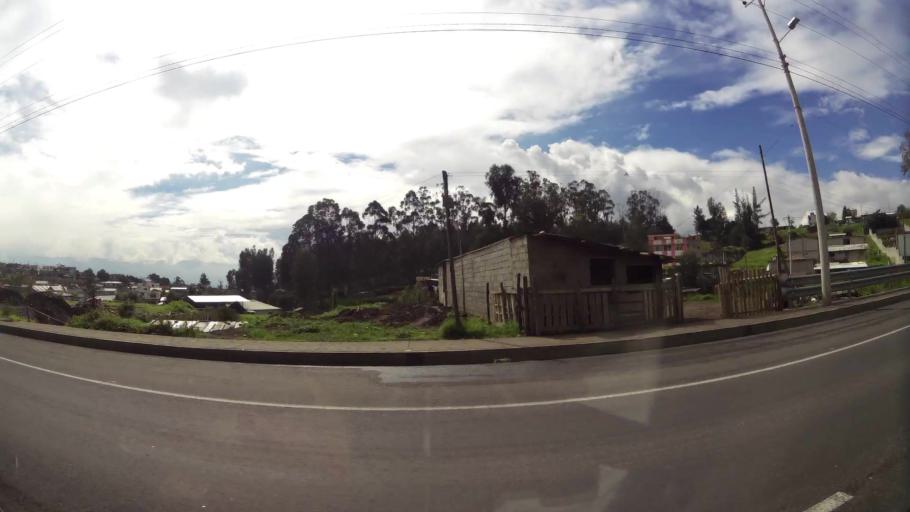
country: EC
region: Pichincha
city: Sangolqui
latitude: -0.3253
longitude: -78.4153
